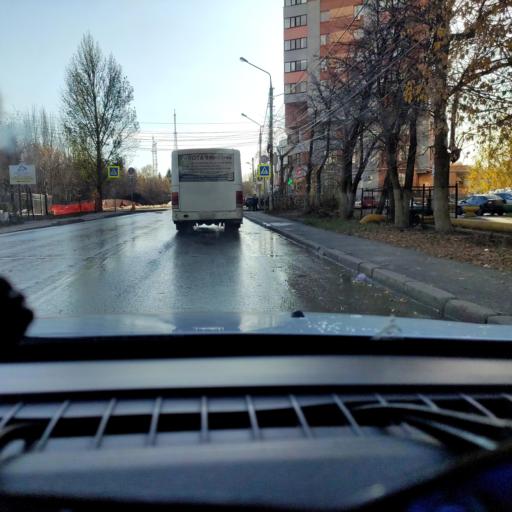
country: RU
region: Samara
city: Samara
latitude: 53.2385
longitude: 50.1806
